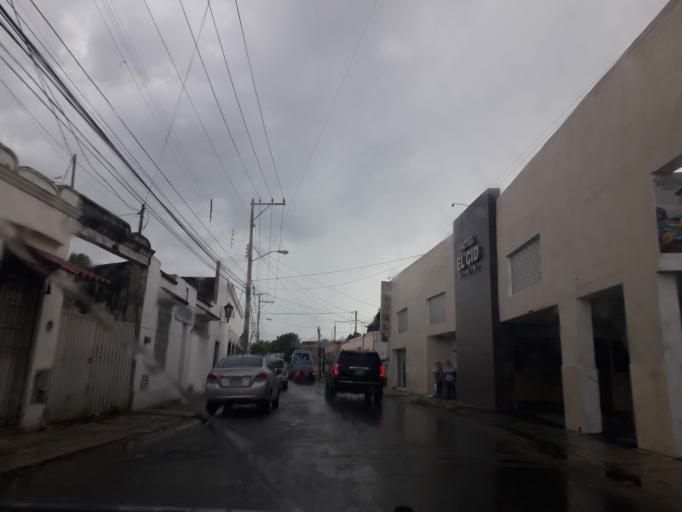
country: MX
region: Yucatan
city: Merida
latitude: 20.9692
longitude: -89.6331
